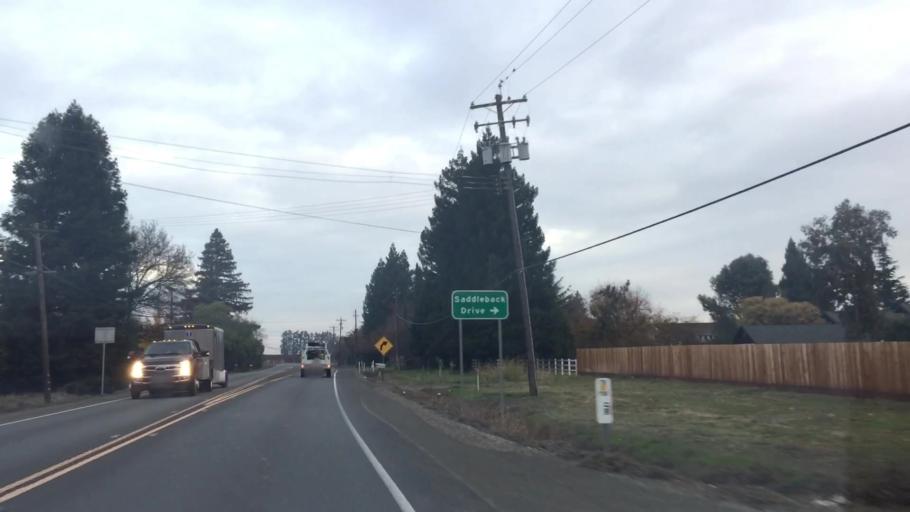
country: US
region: California
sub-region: Yuba County
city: Marysville
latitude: 39.1883
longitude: -121.5941
